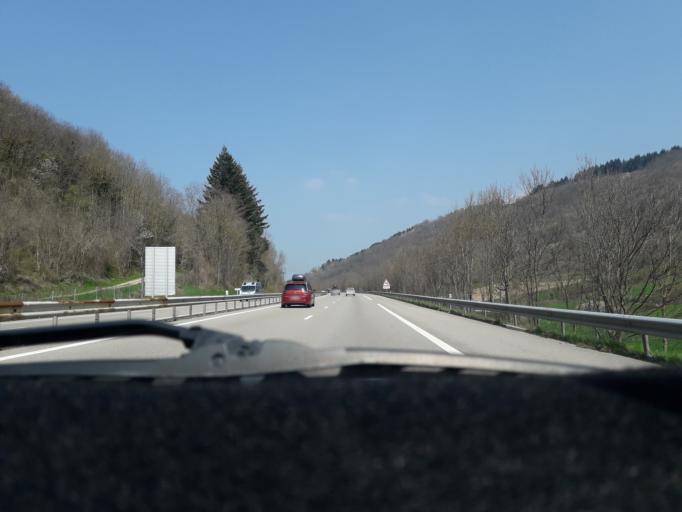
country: FR
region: Rhone-Alpes
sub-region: Departement de l'Isere
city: Colombe
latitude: 45.4070
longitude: 5.4640
